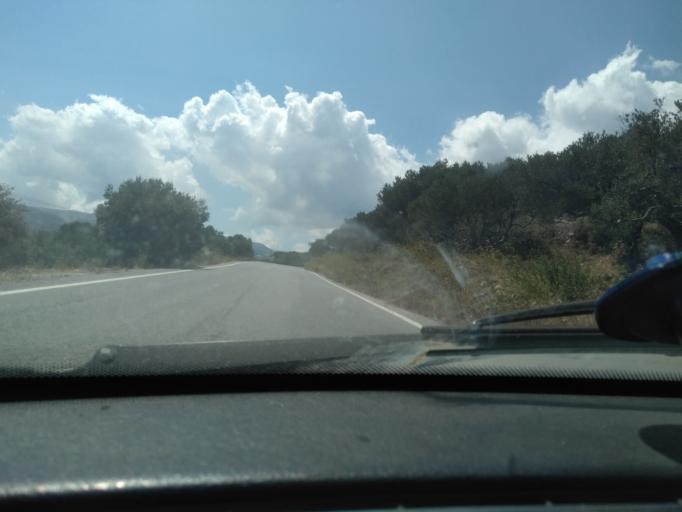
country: GR
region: Crete
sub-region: Nomos Lasithiou
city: Siteia
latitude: 35.1370
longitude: 26.0753
